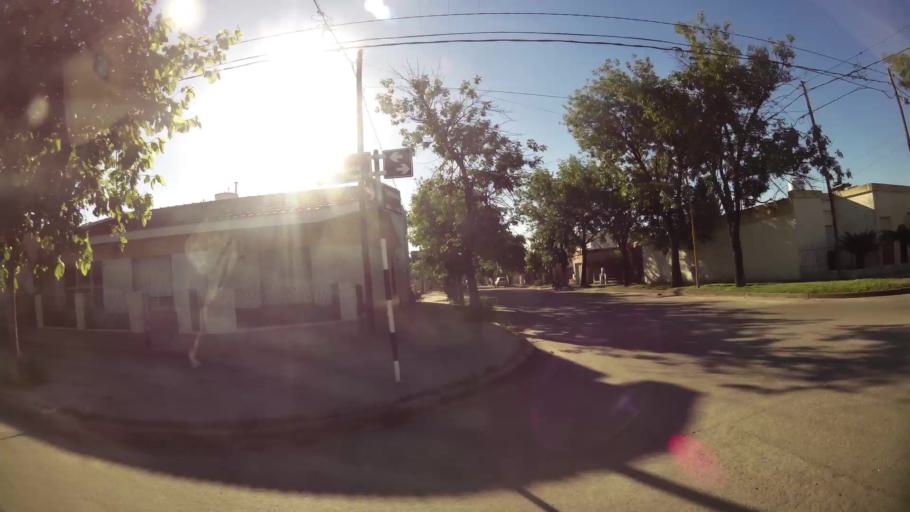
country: AR
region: Cordoba
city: San Francisco
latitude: -31.4423
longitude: -62.0948
